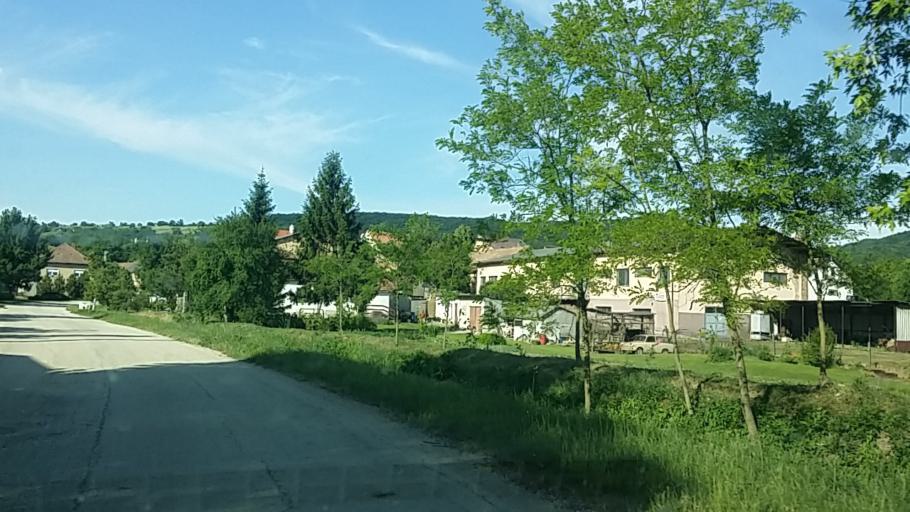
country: HU
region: Komarom-Esztergom
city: Bajna
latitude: 47.6480
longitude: 18.6415
